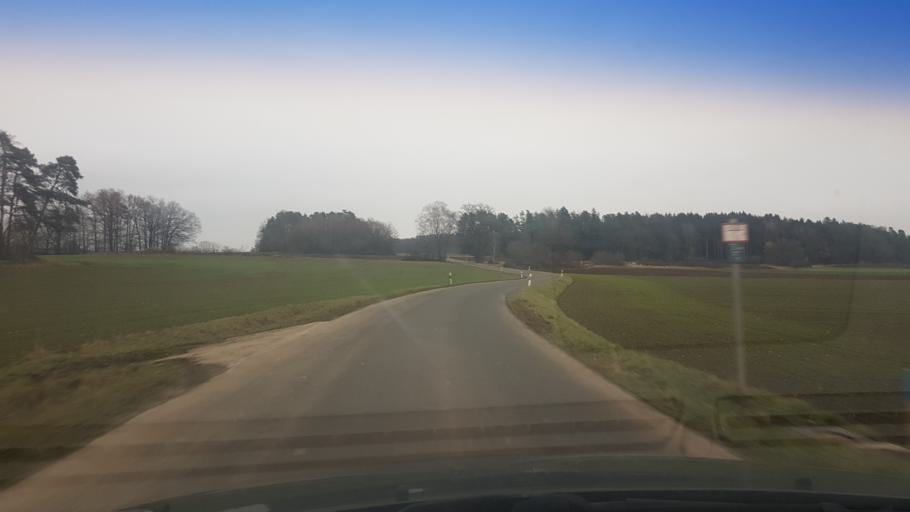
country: DE
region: Bavaria
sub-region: Upper Franconia
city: Stadelhofen
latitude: 50.0290
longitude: 11.2438
